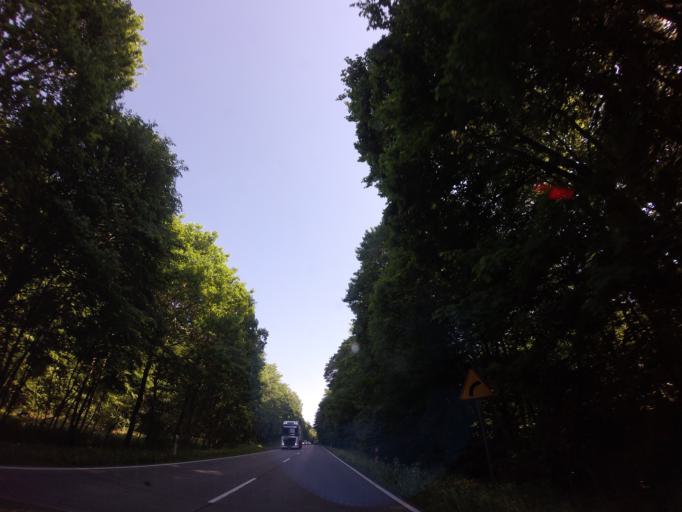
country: PL
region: West Pomeranian Voivodeship
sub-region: Powiat gryfinski
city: Stare Czarnowo
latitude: 53.3228
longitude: 14.7883
